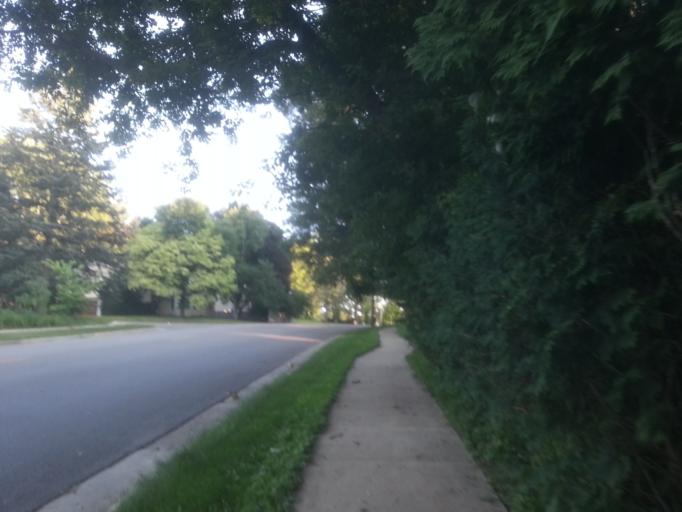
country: US
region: Wisconsin
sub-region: Dane County
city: Shorewood Hills
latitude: 43.0697
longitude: -89.4781
